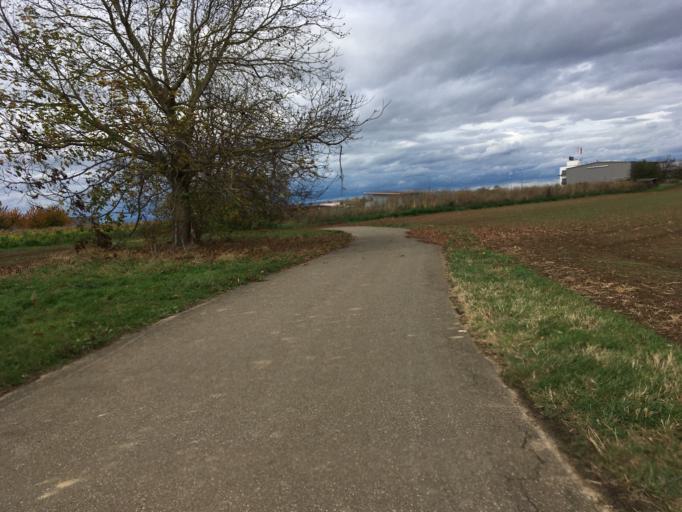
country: DE
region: Baden-Wuerttemberg
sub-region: Freiburg Region
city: Endingen
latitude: 48.1472
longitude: 7.6901
